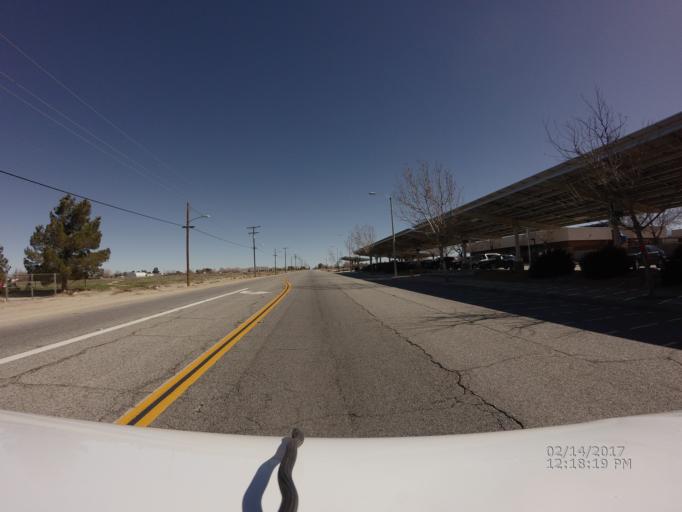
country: US
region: California
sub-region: Los Angeles County
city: Littlerock
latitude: 34.5798
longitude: -117.9586
